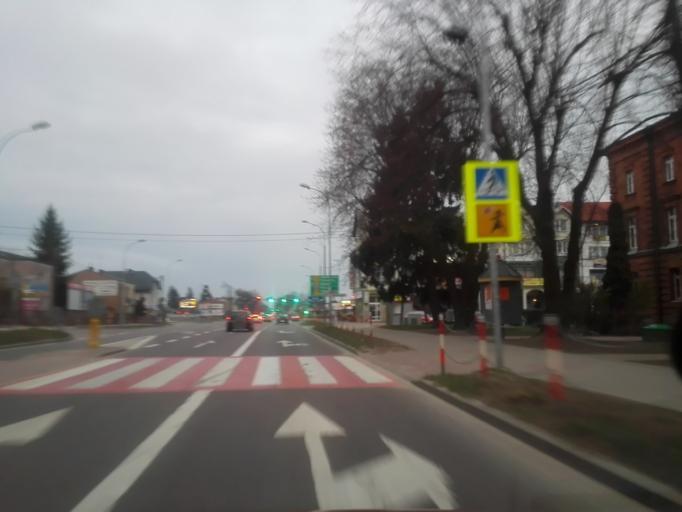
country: PL
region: Podlasie
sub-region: Lomza
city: Lomza
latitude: 53.1747
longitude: 22.0698
